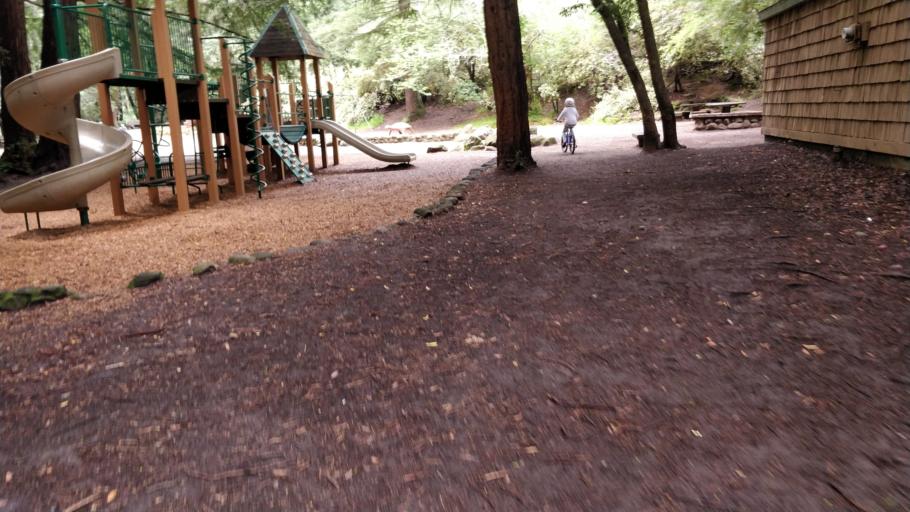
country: US
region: California
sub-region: Marin County
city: Mill Valley
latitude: 37.9051
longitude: -122.5518
